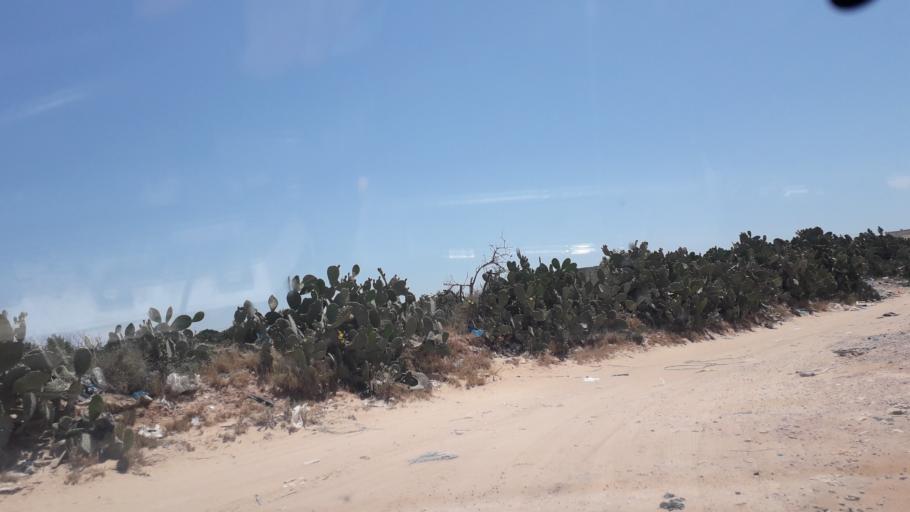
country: TN
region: Safaqis
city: Al Qarmadah
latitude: 34.8313
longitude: 10.7786
